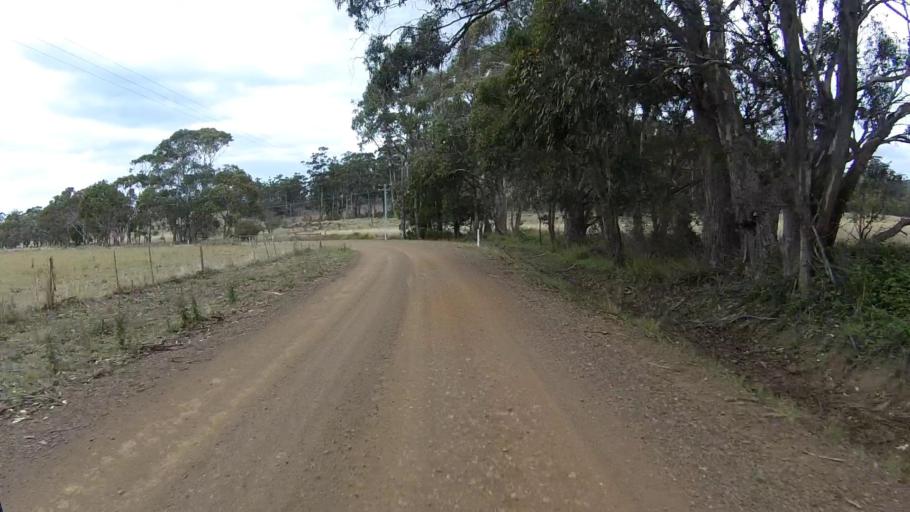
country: AU
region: Tasmania
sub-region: Sorell
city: Sorell
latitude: -42.6545
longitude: 147.9156
